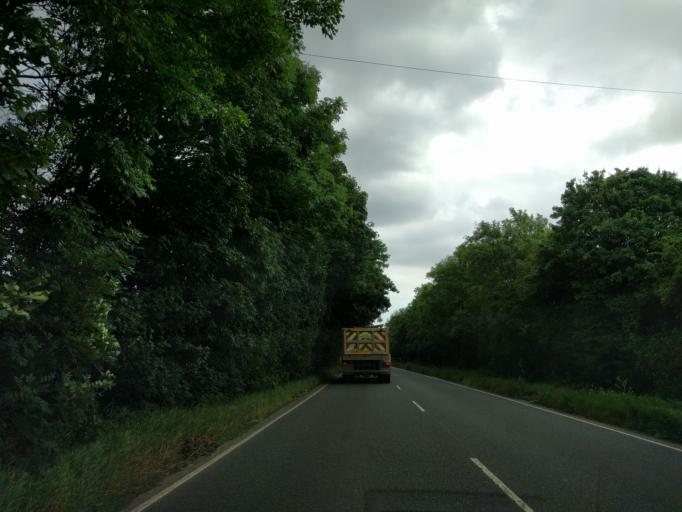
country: GB
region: England
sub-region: Cambridgeshire
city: Needingworth
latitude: 52.3270
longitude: -0.0630
